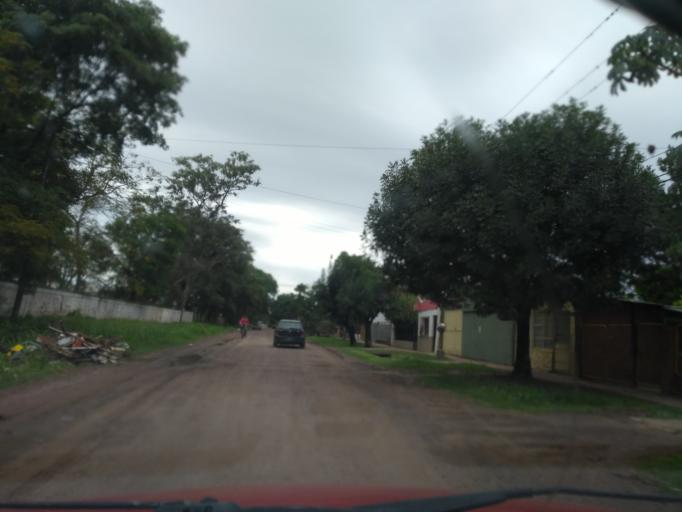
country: AR
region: Chaco
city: Barranqueras
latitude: -27.4777
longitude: -58.9590
